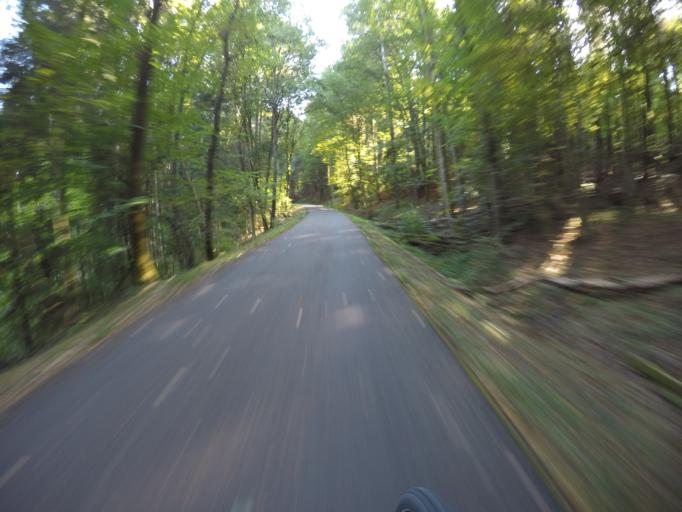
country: DE
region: Baden-Wuerttemberg
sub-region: Regierungsbezirk Stuttgart
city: Steinenbronn
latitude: 48.6797
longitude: 9.1251
